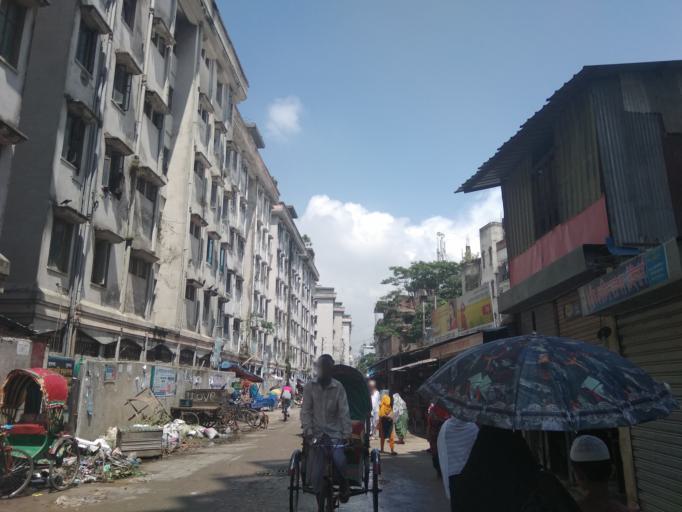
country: BD
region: Dhaka
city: Azimpur
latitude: 23.7996
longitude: 90.3812
